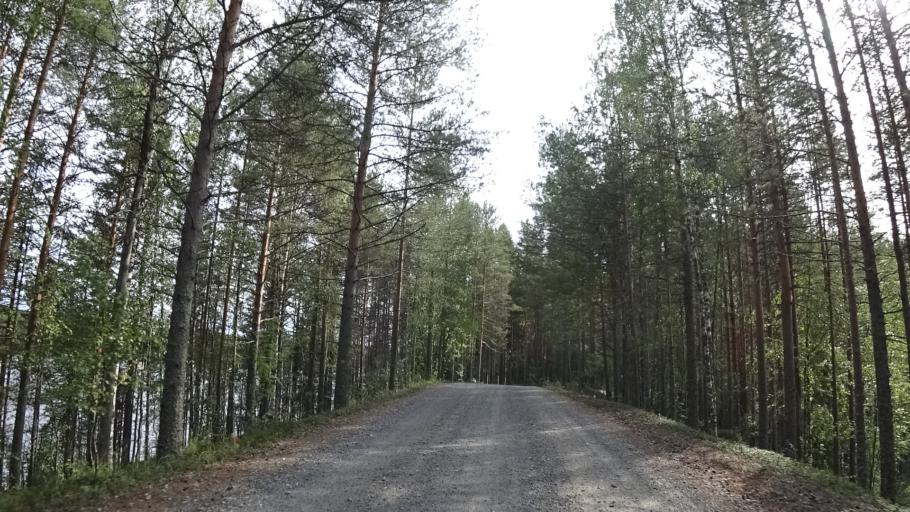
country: FI
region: North Karelia
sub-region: Joensuu
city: Ilomantsi
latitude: 62.6146
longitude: 31.1960
